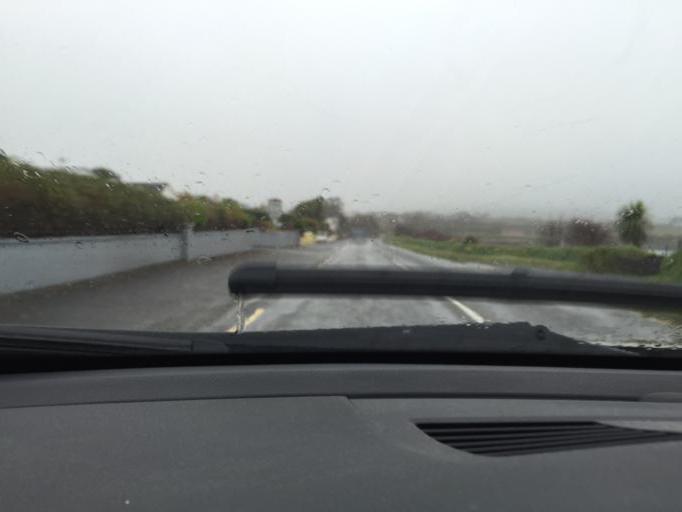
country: IE
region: Munster
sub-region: Ciarrai
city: Dingle
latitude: 52.1341
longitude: -10.3037
